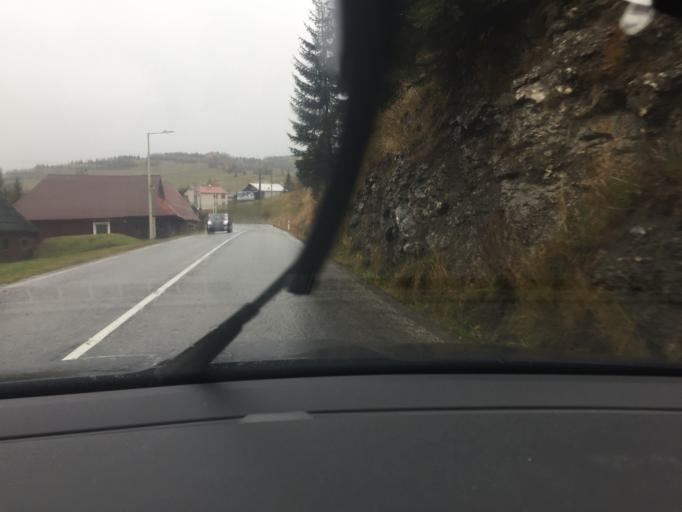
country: SK
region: Presovsky
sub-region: Okres Poprad
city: Zdiar
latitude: 49.2697
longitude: 20.2818
